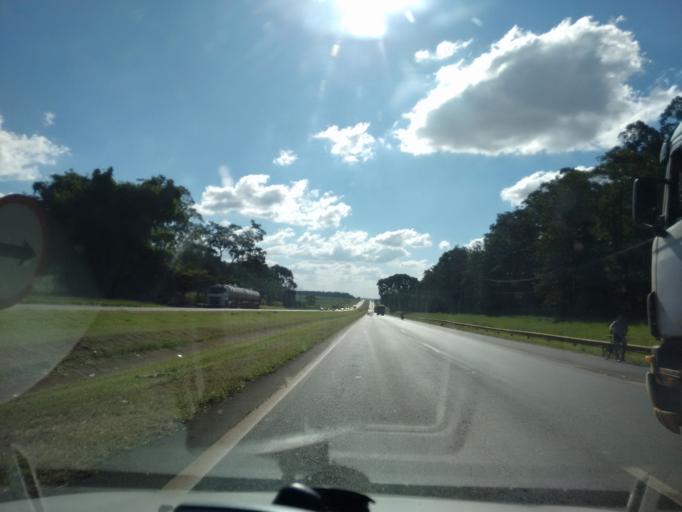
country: BR
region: Sao Paulo
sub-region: Araraquara
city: Araraquara
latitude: -21.8338
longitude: -48.1570
